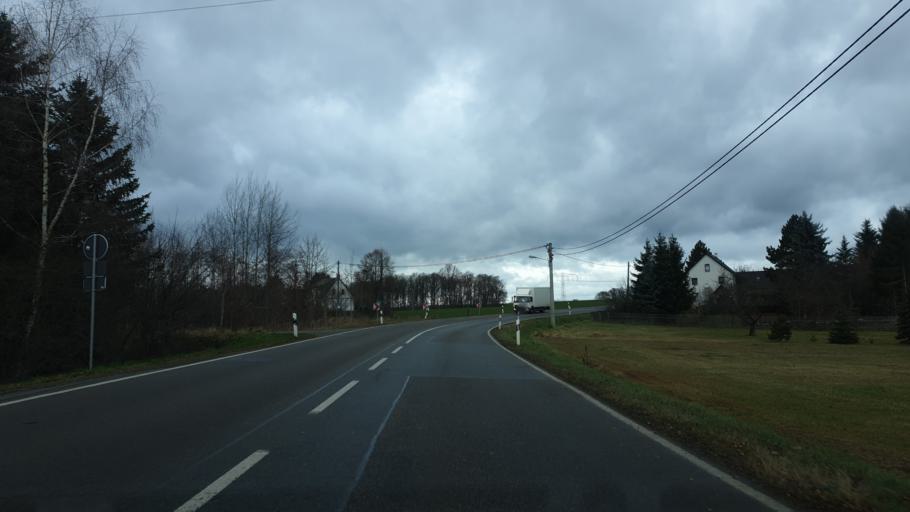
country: DE
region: Saxony
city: Bernsdorf
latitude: 50.8078
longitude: 12.6669
